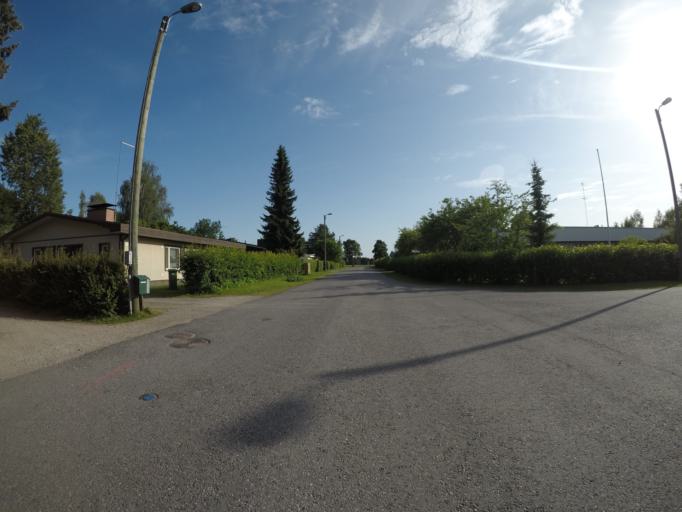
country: FI
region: Haeme
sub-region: Haemeenlinna
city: Haemeenlinna
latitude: 60.9783
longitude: 24.4201
